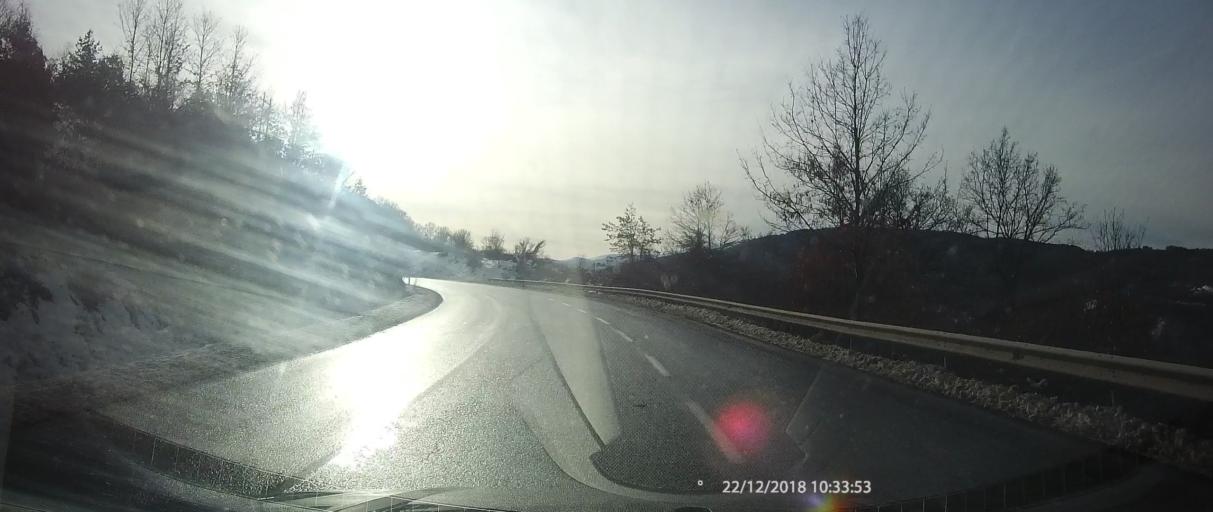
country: MK
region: Kriva Palanka
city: Kriva Palanka
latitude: 42.2186
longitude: 22.4445
